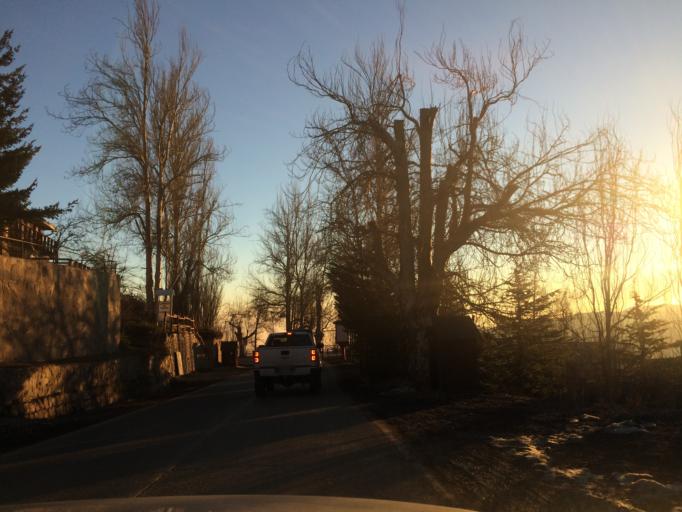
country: CL
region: Santiago Metropolitan
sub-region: Provincia de Santiago
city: Villa Presidente Frei, Nunoa, Santiago, Chile
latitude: -33.3508
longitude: -70.3143
